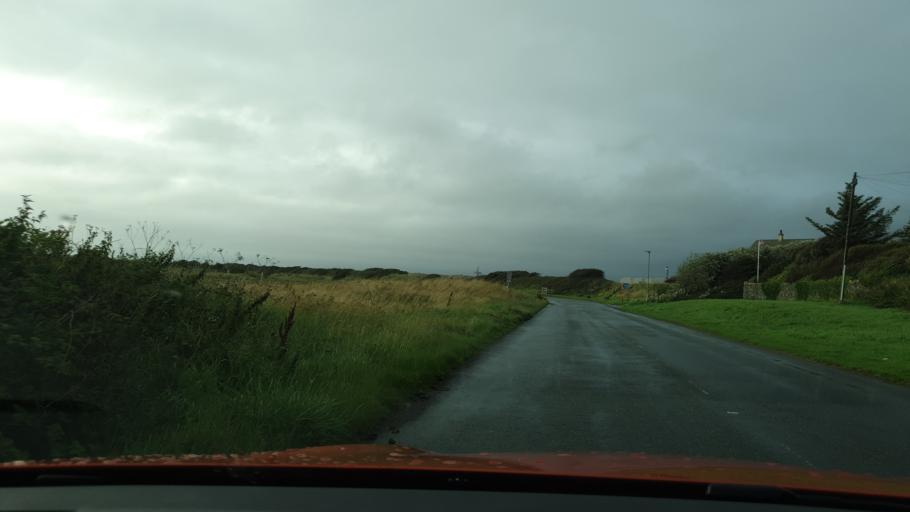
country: GB
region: England
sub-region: Cumbria
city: Barrow in Furness
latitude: 54.0848
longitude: -3.2383
